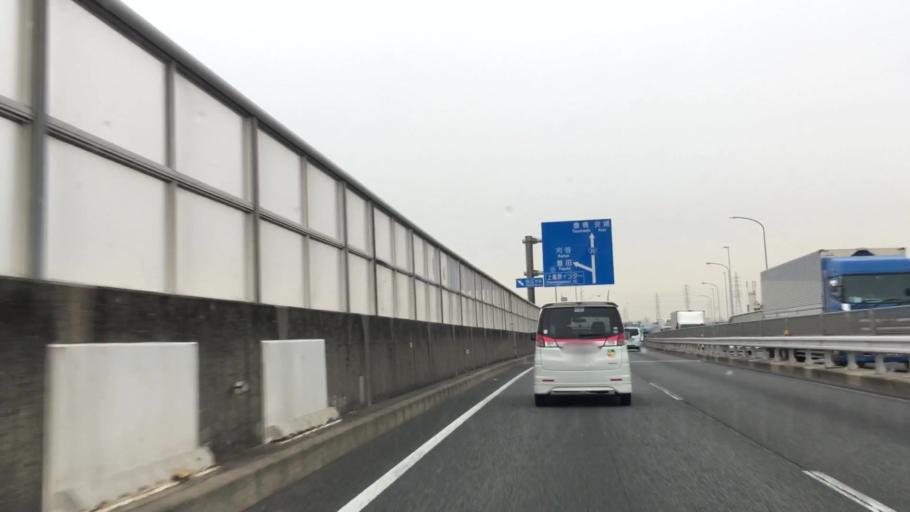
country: JP
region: Aichi
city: Chiryu
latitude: 35.0096
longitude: 137.0254
